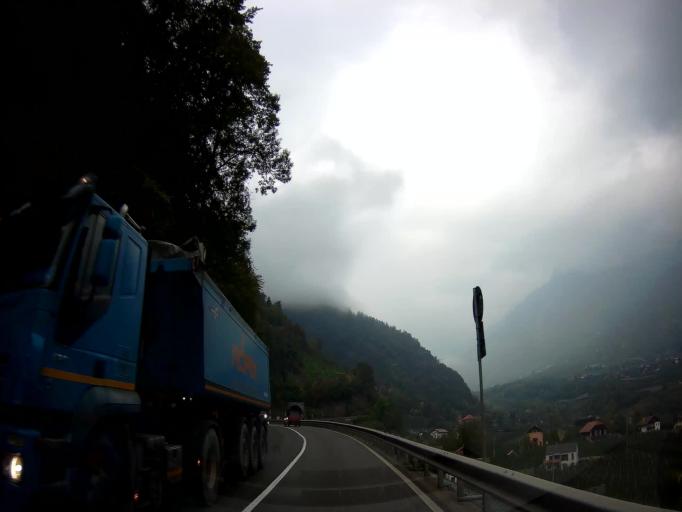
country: IT
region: Trentino-Alto Adige
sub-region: Bolzano
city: Lagundo
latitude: 46.6760
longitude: 11.1111
